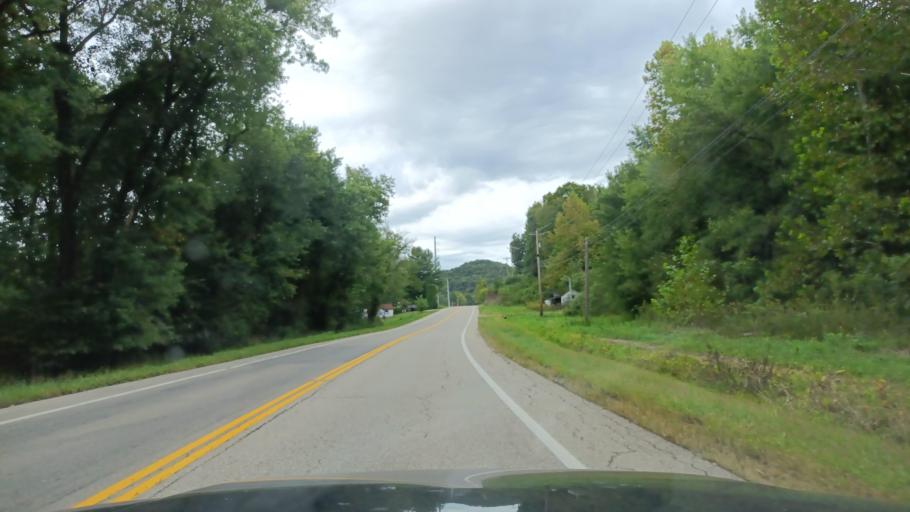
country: US
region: Ohio
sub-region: Vinton County
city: McArthur
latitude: 39.2378
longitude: -82.4502
